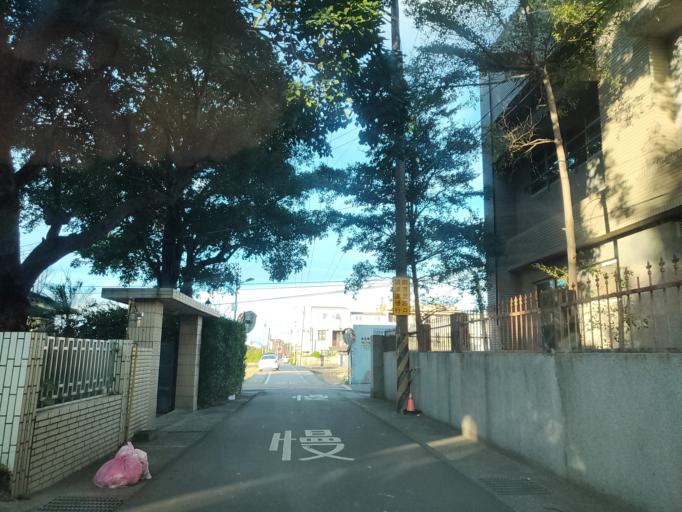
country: TW
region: Taiwan
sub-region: Miaoli
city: Miaoli
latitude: 24.5578
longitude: 120.8319
